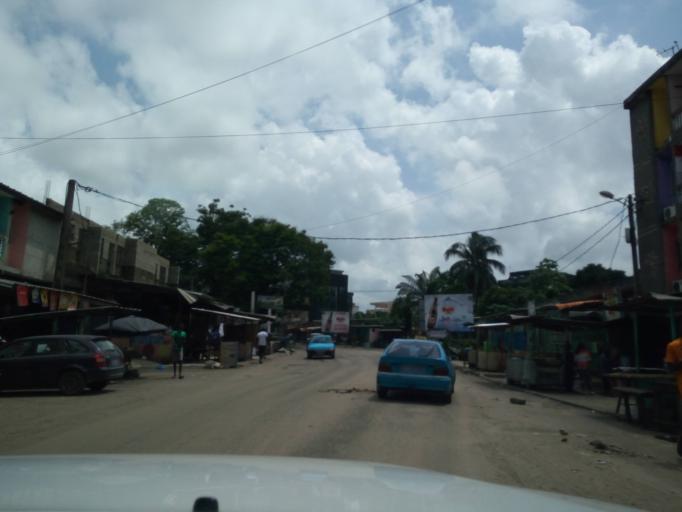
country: CI
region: Lagunes
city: Abidjan
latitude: 5.3406
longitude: -4.0981
